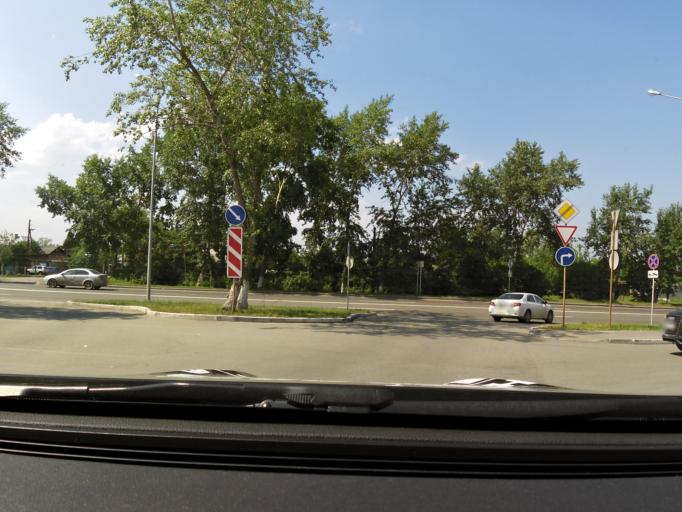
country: RU
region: Sverdlovsk
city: Shirokaya Rechka
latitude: 56.8181
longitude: 60.5365
